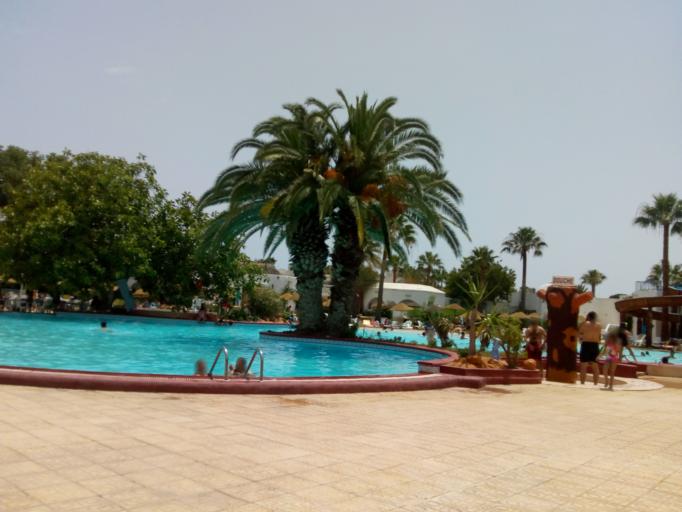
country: TN
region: Nabul
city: Al Hammamat
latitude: 36.3936
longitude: 10.5562
